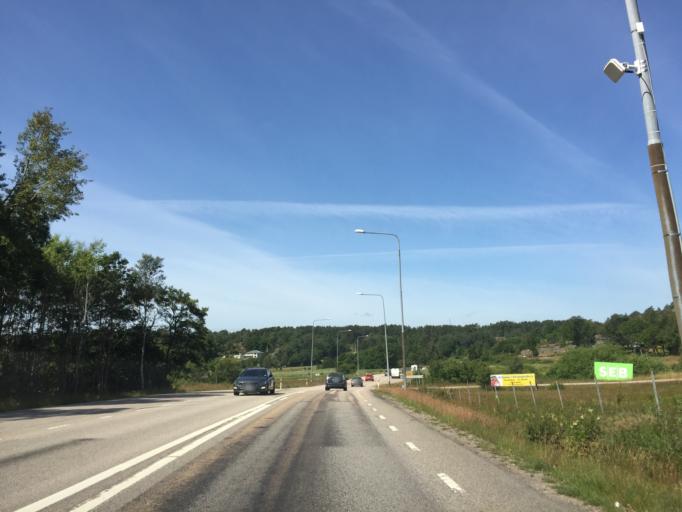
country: SE
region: Vaestra Goetaland
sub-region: Lysekils Kommun
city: Lysekil
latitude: 58.3028
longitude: 11.4992
